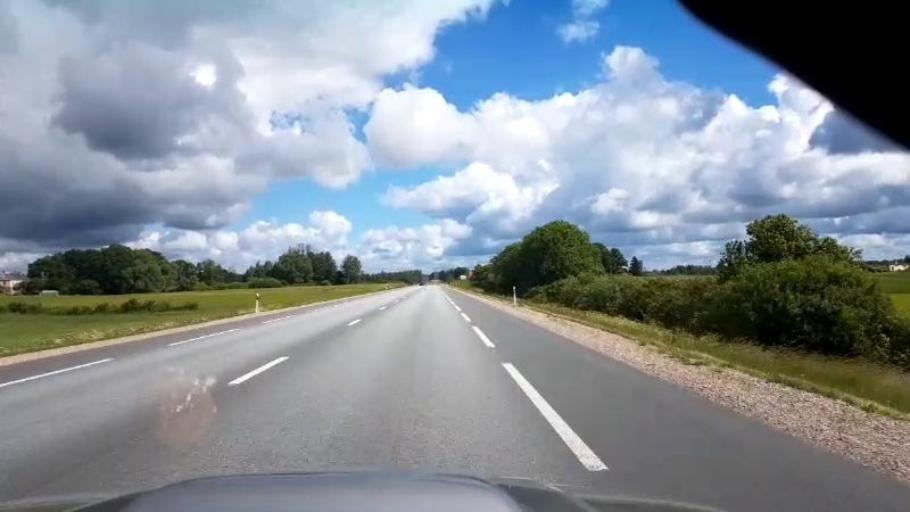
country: LV
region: Lecava
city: Iecava
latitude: 56.6190
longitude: 24.2175
